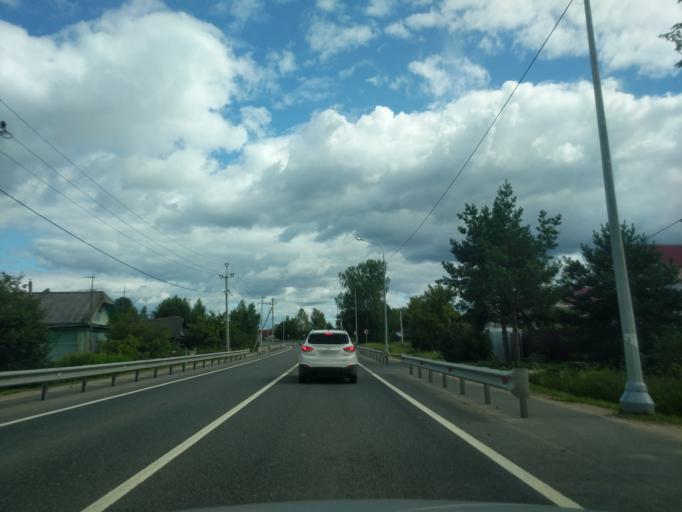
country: RU
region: Kostroma
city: Oktyabr'skiy
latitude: 57.7982
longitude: 41.1998
